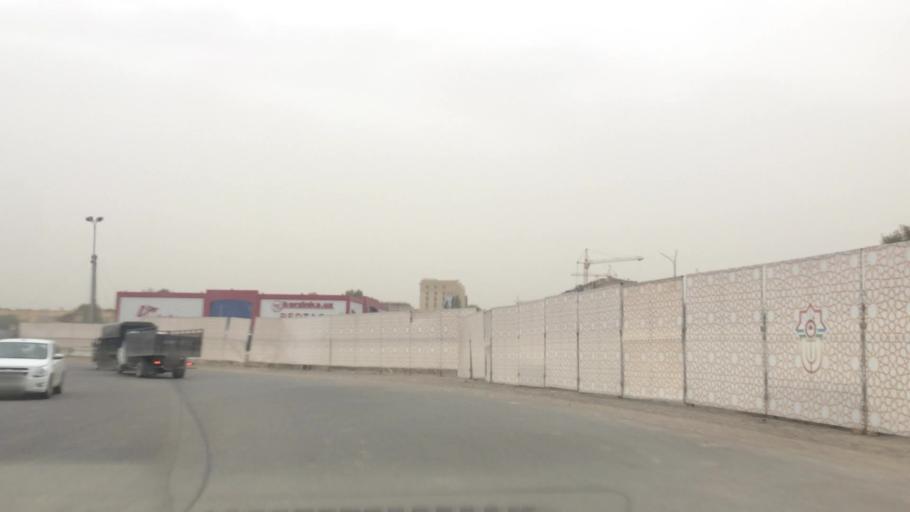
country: UZ
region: Toshkent
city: Salor
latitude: 41.3054
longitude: 69.3405
